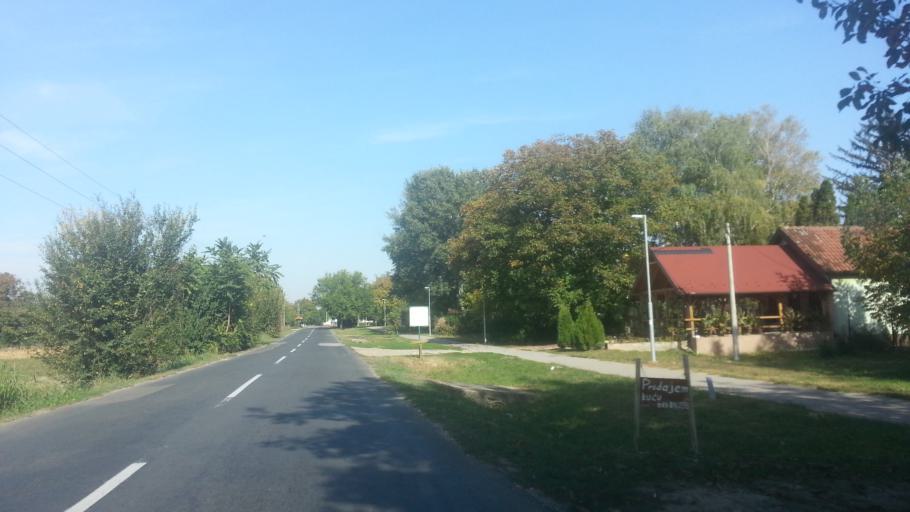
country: RS
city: Belegis
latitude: 45.0073
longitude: 20.3137
